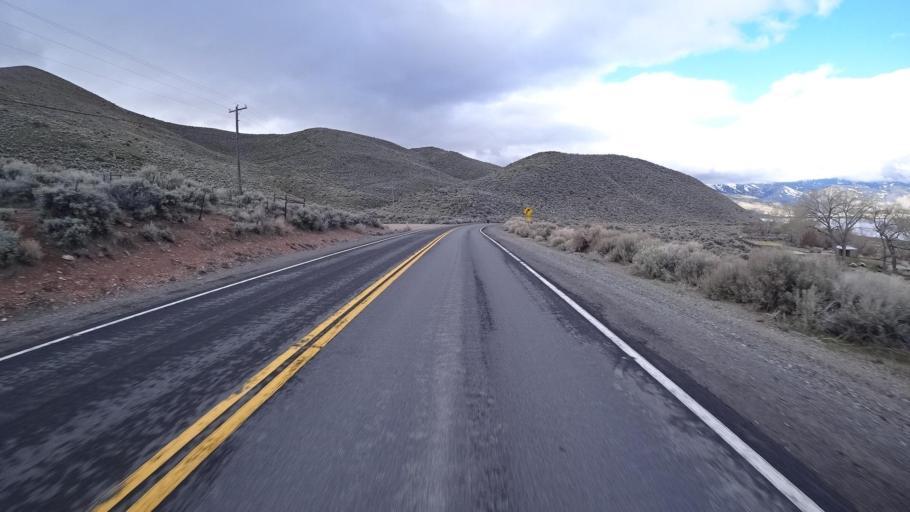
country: US
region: Nevada
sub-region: Carson City
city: Carson City
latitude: 39.2361
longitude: -119.7692
